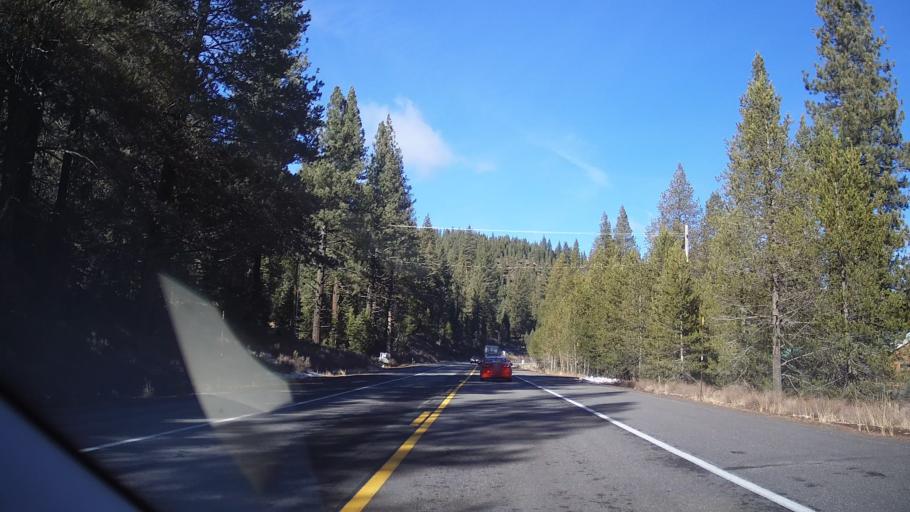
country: US
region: California
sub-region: Nevada County
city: Truckee
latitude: 39.2850
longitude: -120.2079
